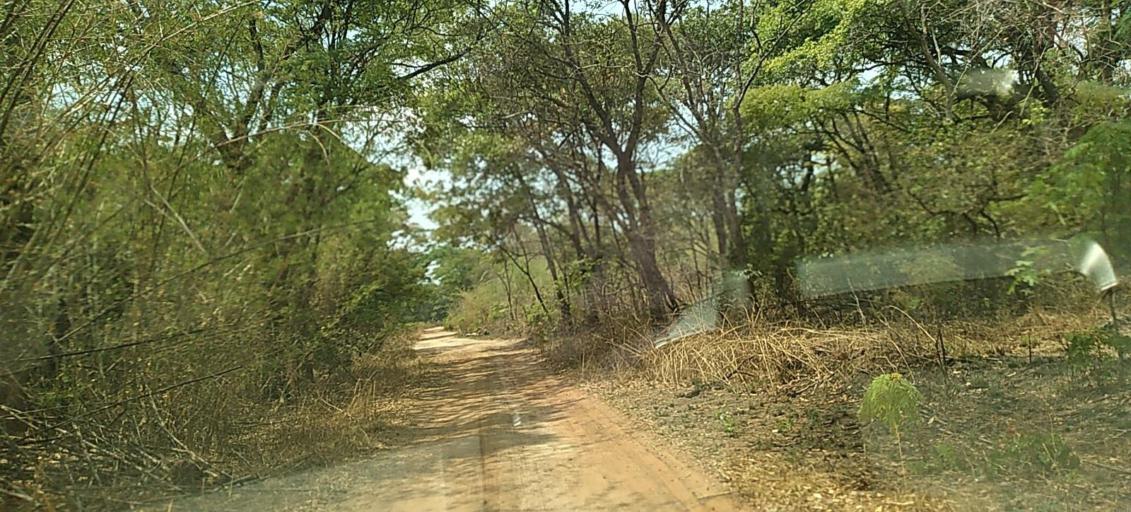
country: ZM
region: Copperbelt
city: Chingola
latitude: -12.7627
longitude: 27.7068
